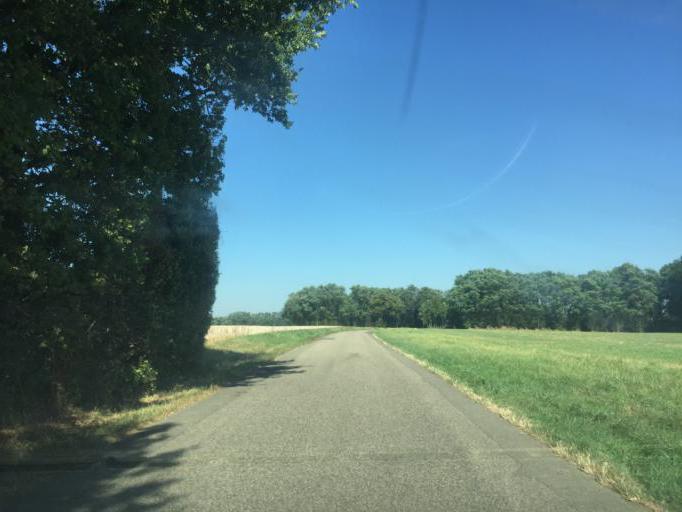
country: FR
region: Rhone-Alpes
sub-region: Departement de l'Ain
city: Saint-Maurice-de-Beynost
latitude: 45.8478
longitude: 4.9733
